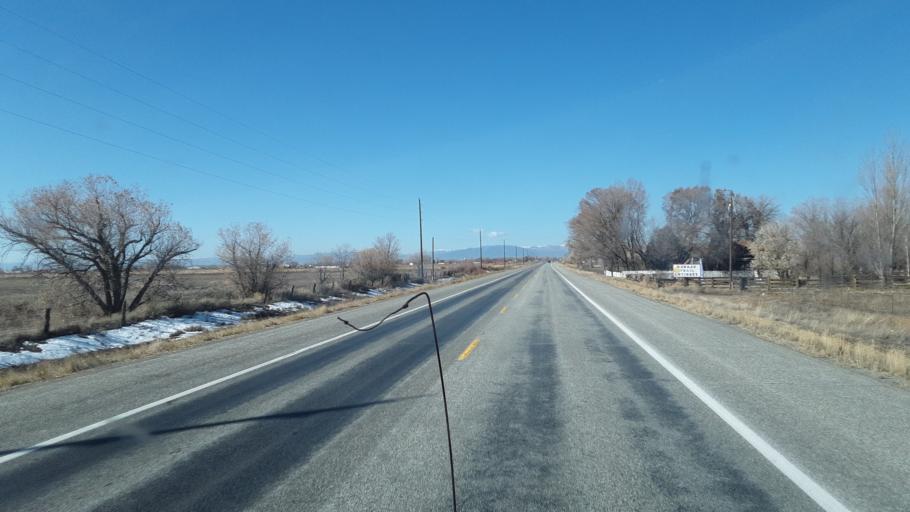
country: US
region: Colorado
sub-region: Alamosa County
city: Alamosa East
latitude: 37.4735
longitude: -105.7907
